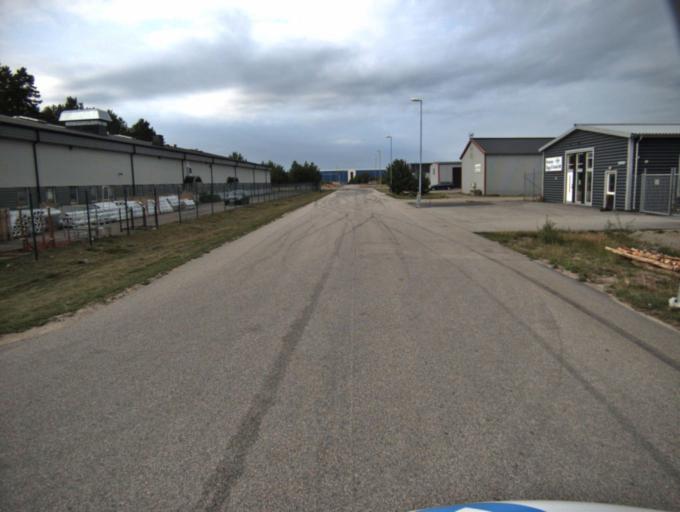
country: SE
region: Vaestra Goetaland
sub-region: Ulricehamns Kommun
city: Ulricehamn
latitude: 57.8326
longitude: 13.4248
